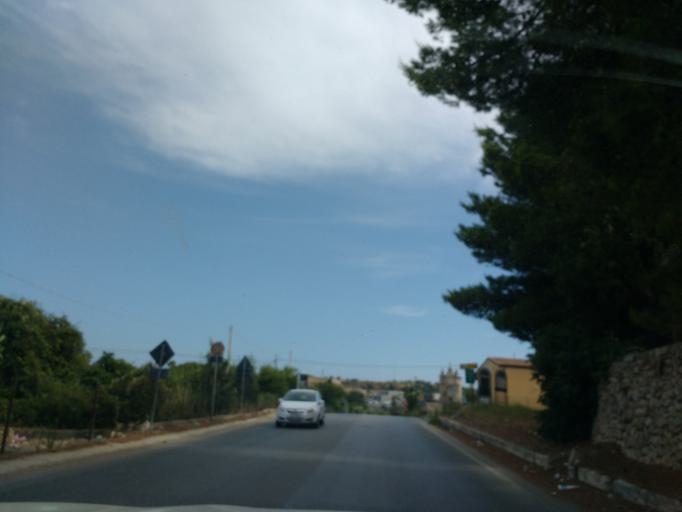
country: IT
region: Sicily
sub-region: Provincia di Siracusa
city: Noto
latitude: 36.8847
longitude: 15.0627
